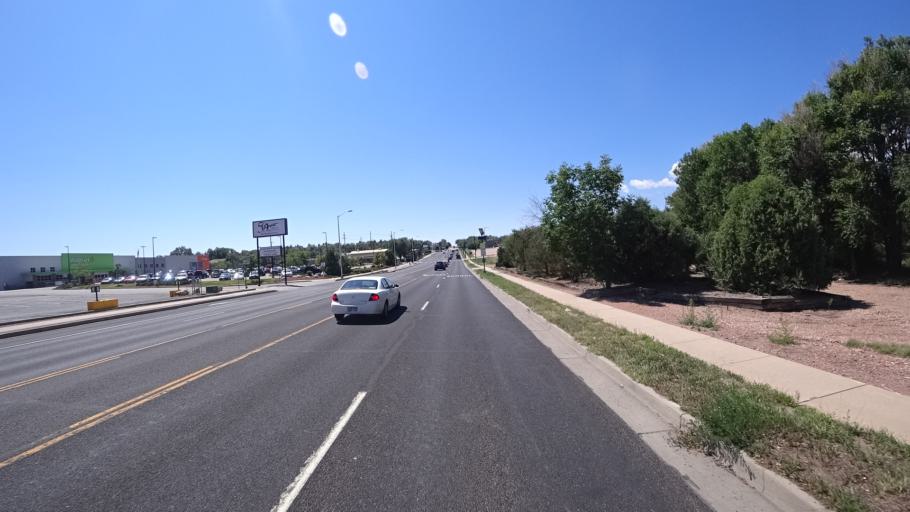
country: US
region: Colorado
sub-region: El Paso County
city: Colorado Springs
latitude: 38.8584
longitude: -104.7943
